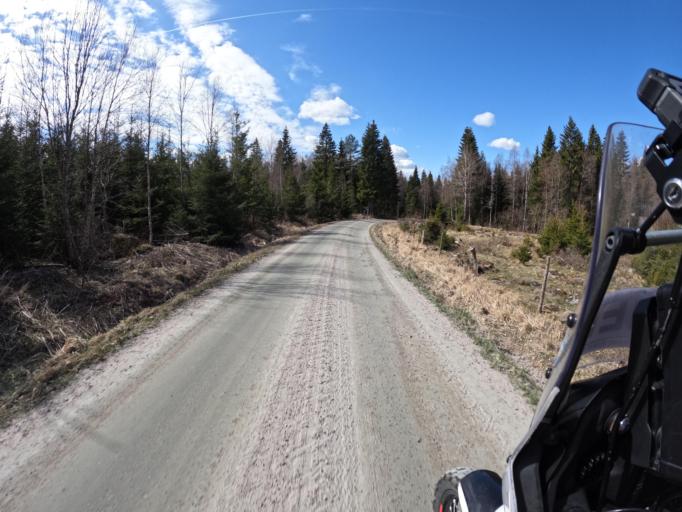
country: SE
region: Vaestra Goetaland
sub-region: Ulricehamns Kommun
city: Ulricehamn
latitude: 57.9184
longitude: 13.5174
